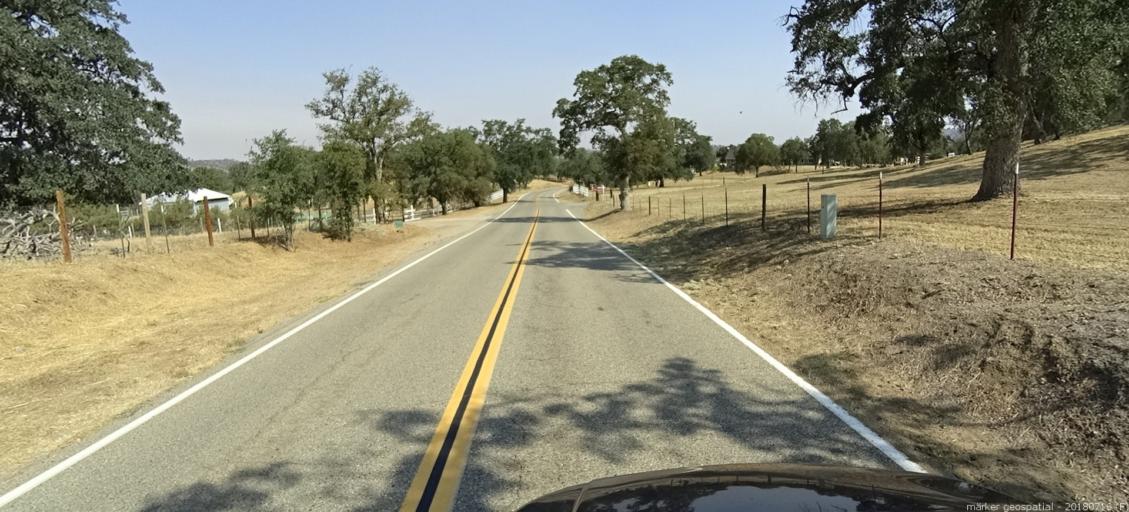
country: US
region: California
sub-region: Madera County
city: Yosemite Lakes
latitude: 37.2318
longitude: -119.7676
